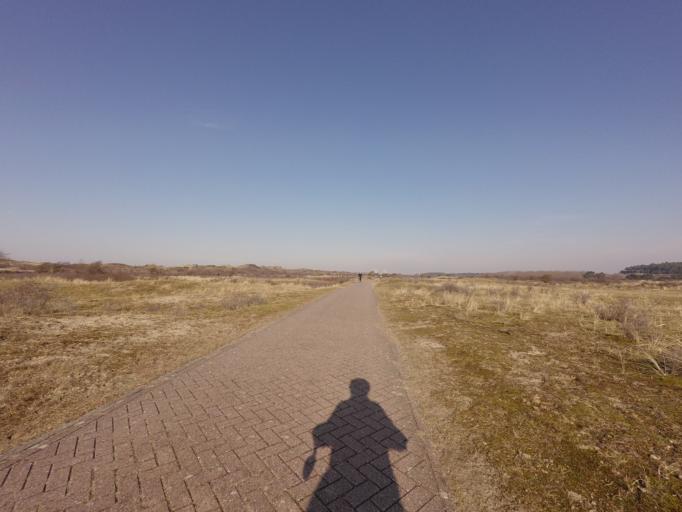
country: NL
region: North Holland
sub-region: Gemeente Bloemendaal
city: Bloemendaal
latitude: 52.4213
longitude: 4.5725
